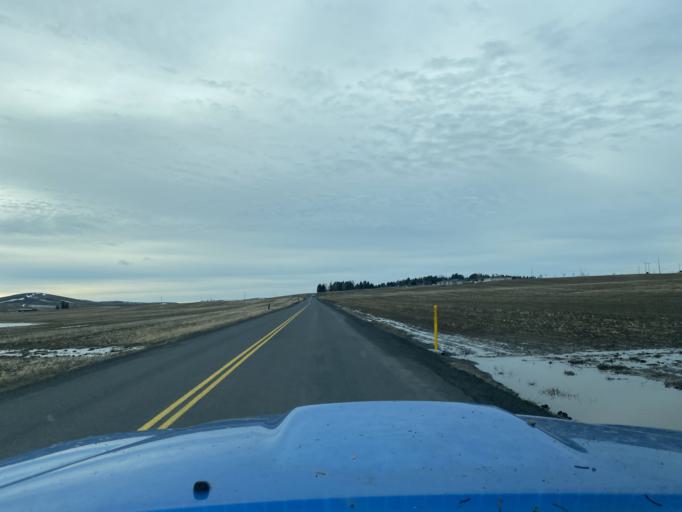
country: US
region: Idaho
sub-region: Latah County
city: Moscow
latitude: 46.7157
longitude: -116.9724
